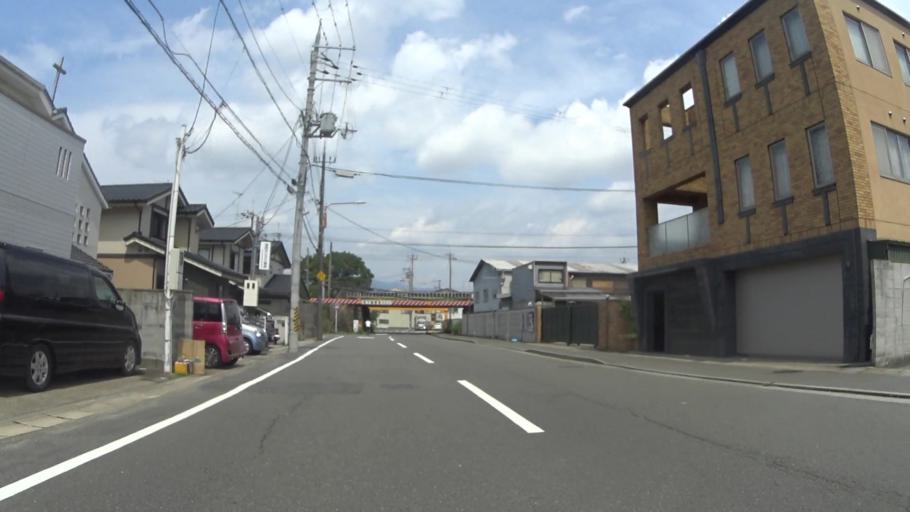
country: JP
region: Kyoto
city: Muko
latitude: 34.9868
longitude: 135.7088
